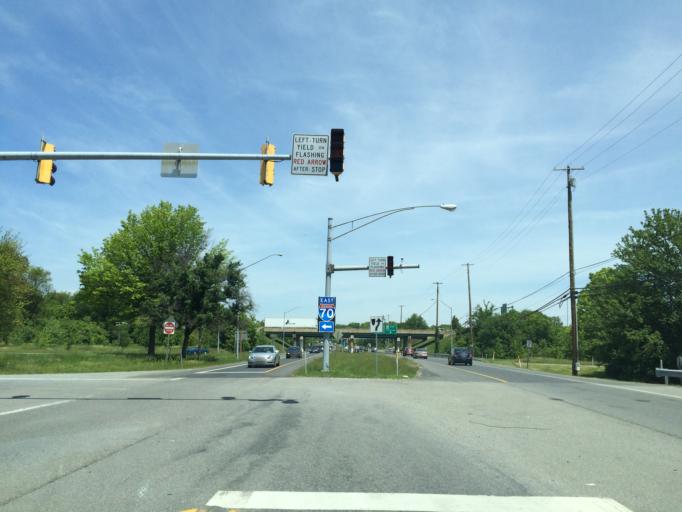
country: US
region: Maryland
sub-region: Washington County
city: Halfway
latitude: 39.6035
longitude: -77.7292
